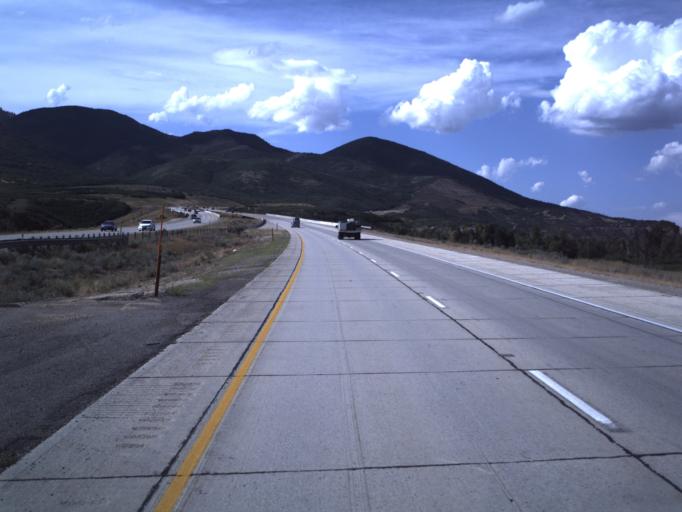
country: US
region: Utah
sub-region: Wasatch County
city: Heber
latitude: 40.5677
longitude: -111.4296
